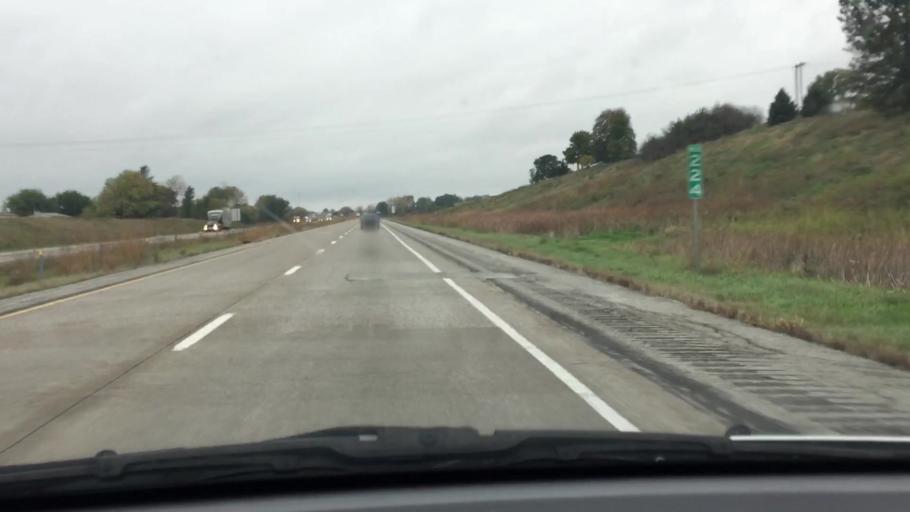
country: US
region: Iowa
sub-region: Iowa County
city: Williamsburg
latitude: 41.6880
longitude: -91.9293
